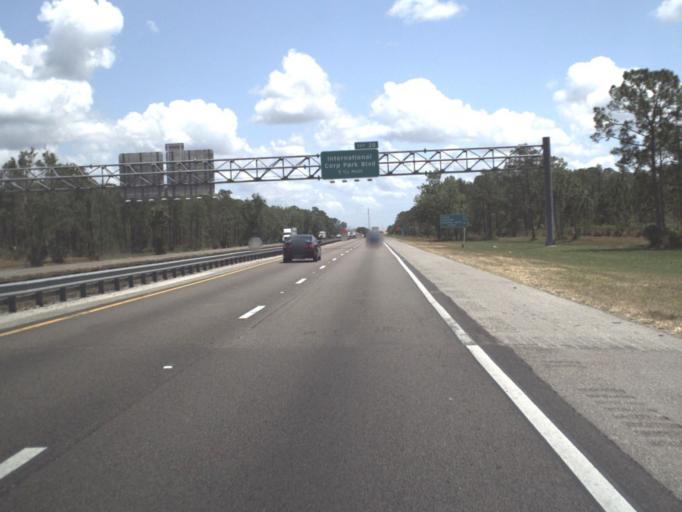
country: US
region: Florida
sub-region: Orange County
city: Alafaya
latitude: 28.4515
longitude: -81.1941
